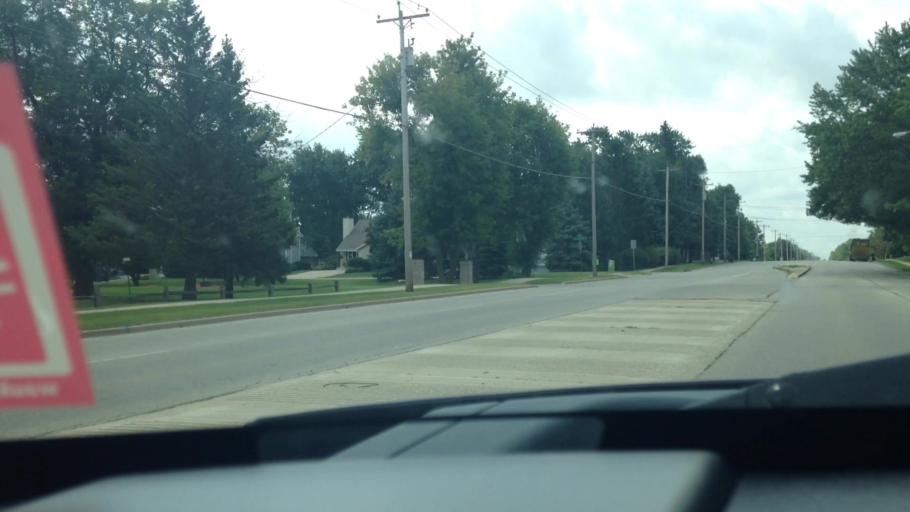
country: US
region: Wisconsin
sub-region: Waukesha County
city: Menomonee Falls
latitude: 43.1614
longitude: -88.1042
